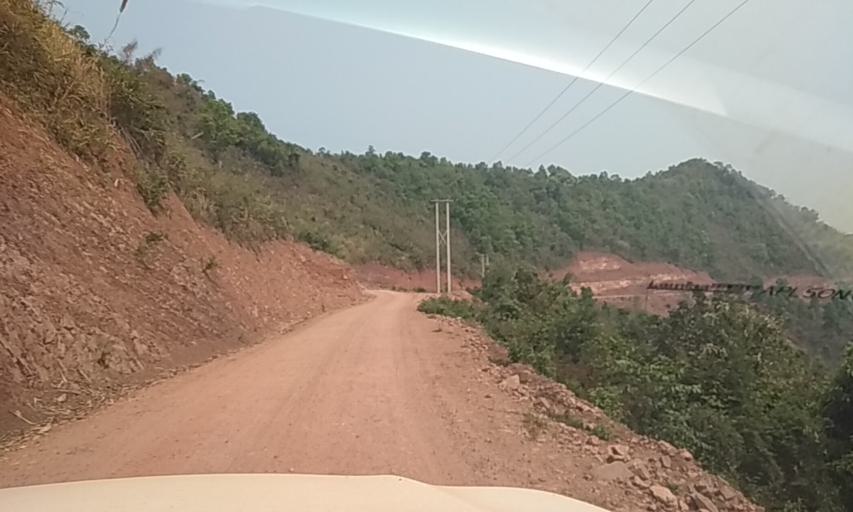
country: VN
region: Huyen Dien Bien
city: Dien Bien Phu
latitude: 21.4960
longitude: 102.7864
